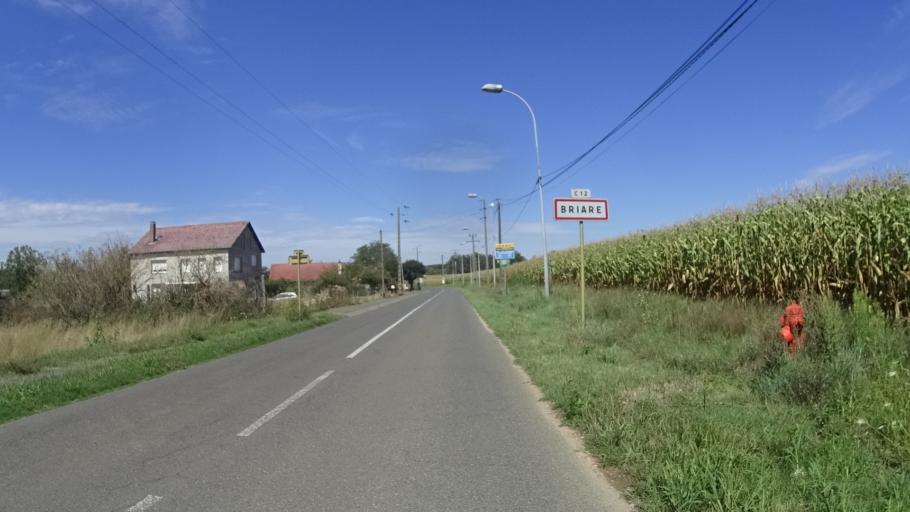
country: FR
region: Centre
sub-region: Departement du Loiret
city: Briare
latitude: 47.6225
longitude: 2.7517
